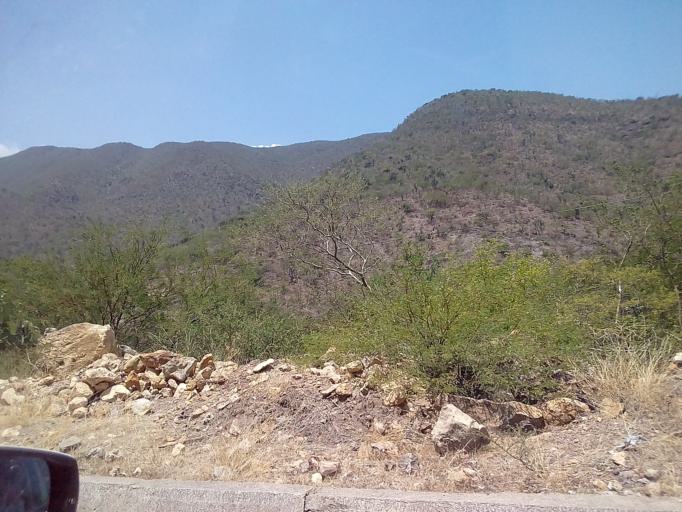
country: MX
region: Oaxaca
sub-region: San Pedro Quiatoni
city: San Pedro Quiatoni
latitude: 16.6729
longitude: -96.1451
